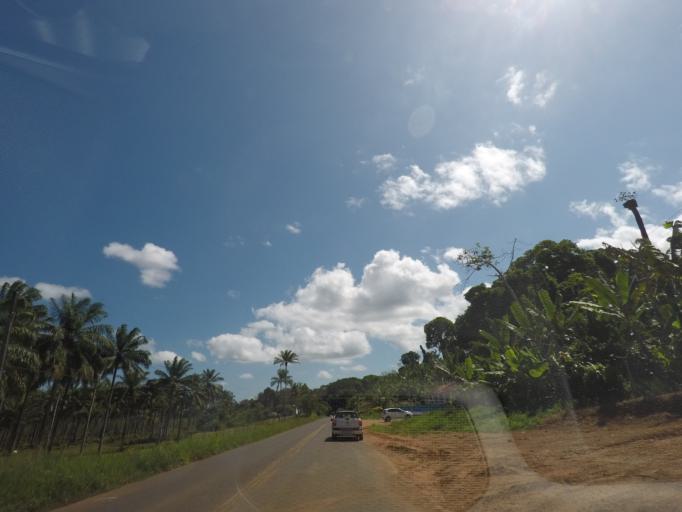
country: BR
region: Bahia
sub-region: Taperoa
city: Taperoa
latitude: -13.5639
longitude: -39.1051
